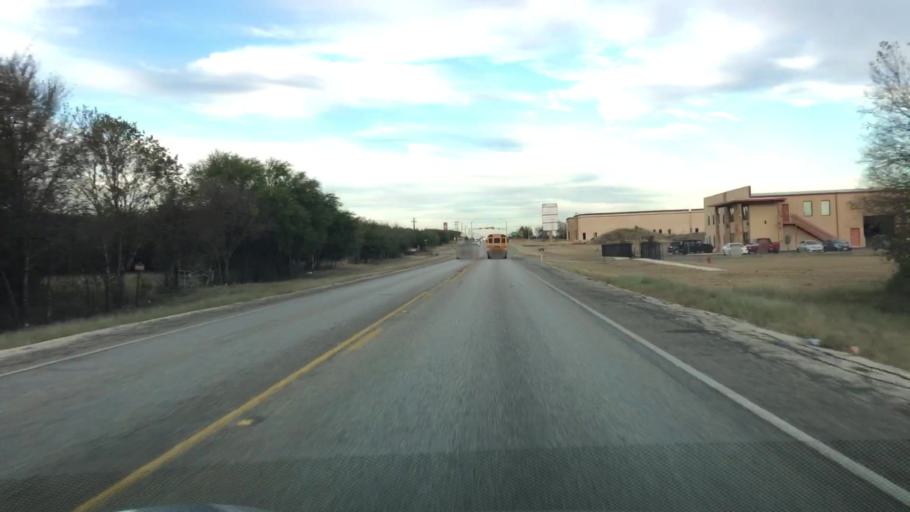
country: US
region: Texas
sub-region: Bexar County
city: Converse
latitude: 29.5241
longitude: -98.3116
